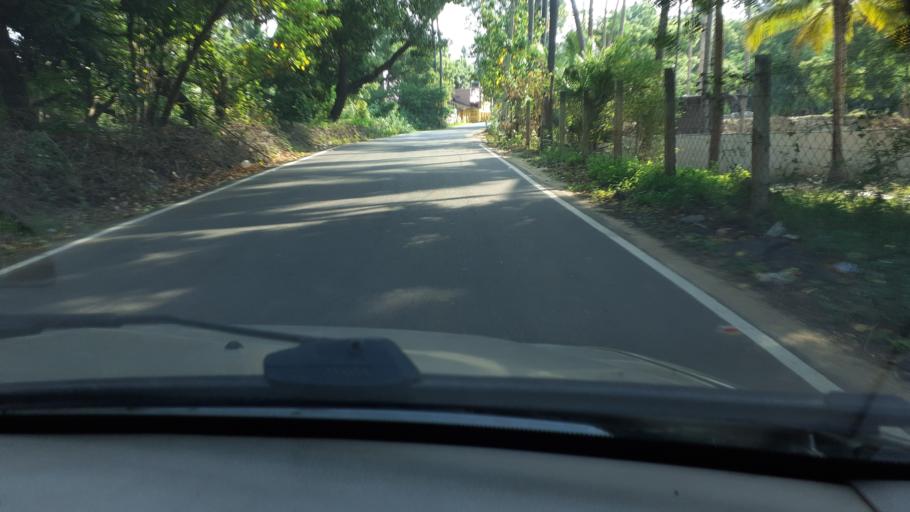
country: IN
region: Tamil Nadu
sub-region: Thoothukkudi
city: Eral
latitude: 8.5802
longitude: 78.0357
